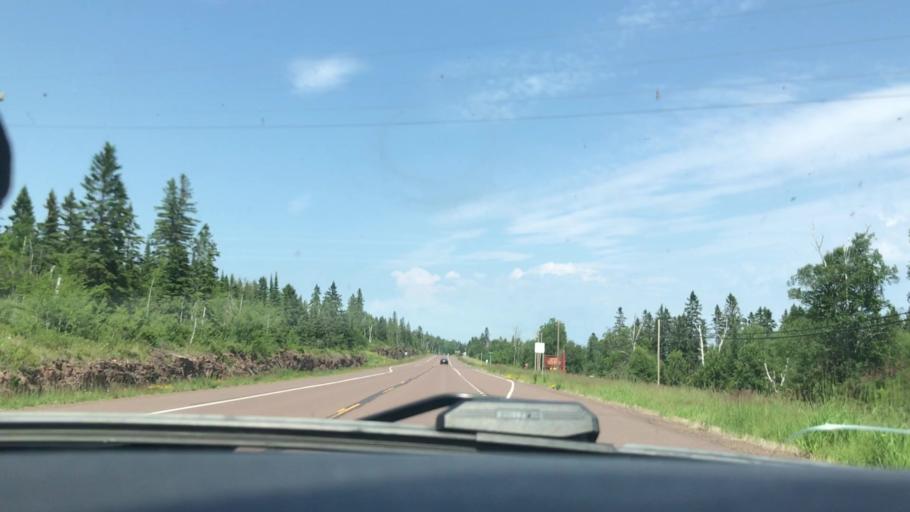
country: US
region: Minnesota
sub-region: Cook County
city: Grand Marais
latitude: 47.6135
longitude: -90.7605
